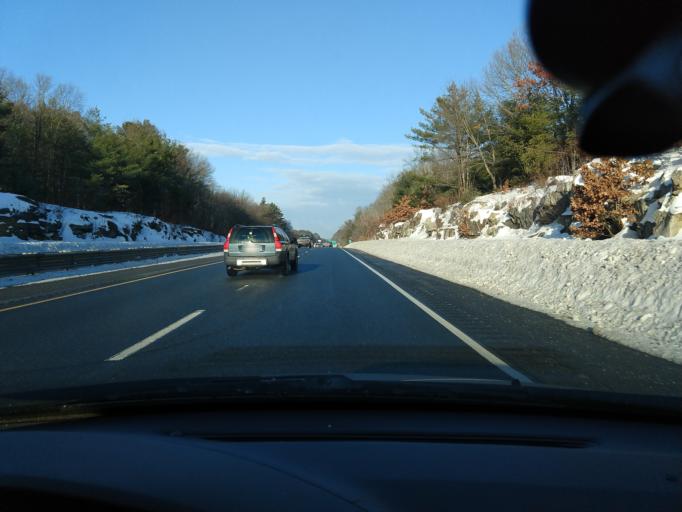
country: US
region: Massachusetts
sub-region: Middlesex County
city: Acton
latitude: 42.4972
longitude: -71.4690
